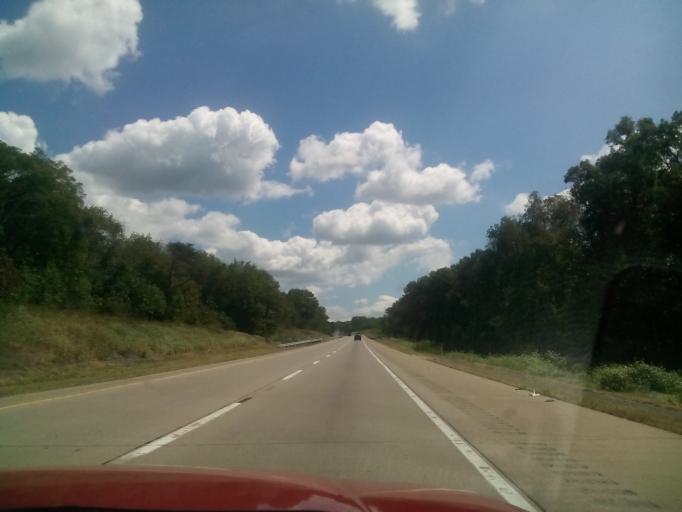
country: US
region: Pennsylvania
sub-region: Northumberland County
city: Riverside
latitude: 40.9879
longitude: -76.7262
